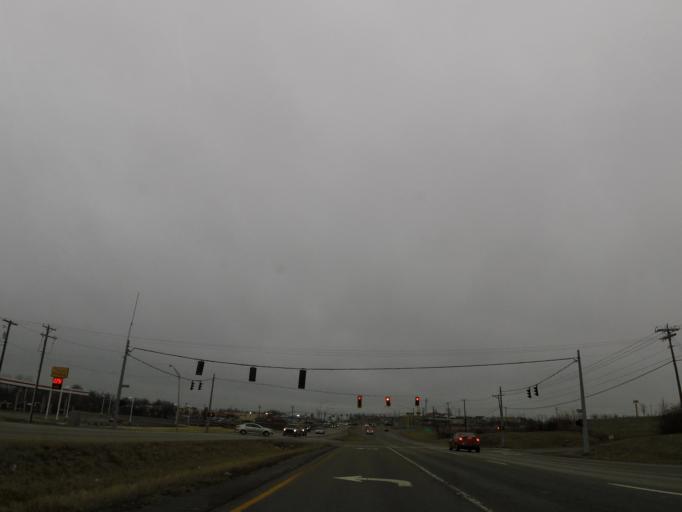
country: US
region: Kentucky
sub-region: Boyle County
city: Danville
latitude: 37.6172
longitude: -84.7782
